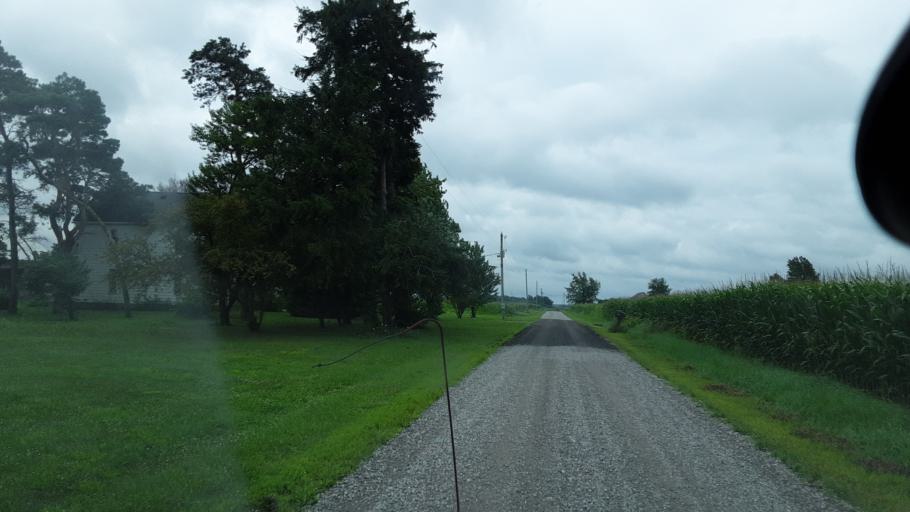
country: US
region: Indiana
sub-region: Wells County
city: Ossian
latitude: 40.8433
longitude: -85.0818
